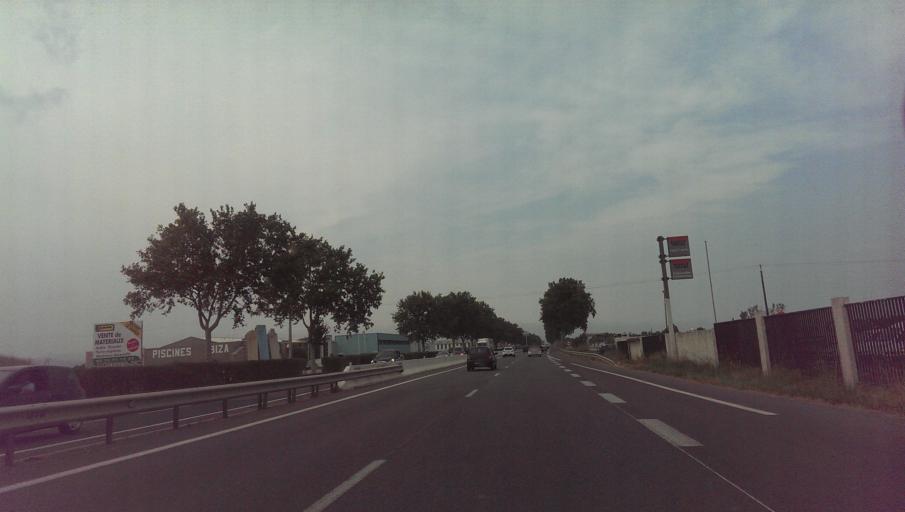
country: FR
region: Languedoc-Roussillon
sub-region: Departement des Pyrenees-Orientales
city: Pia
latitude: 42.7565
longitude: 2.8966
